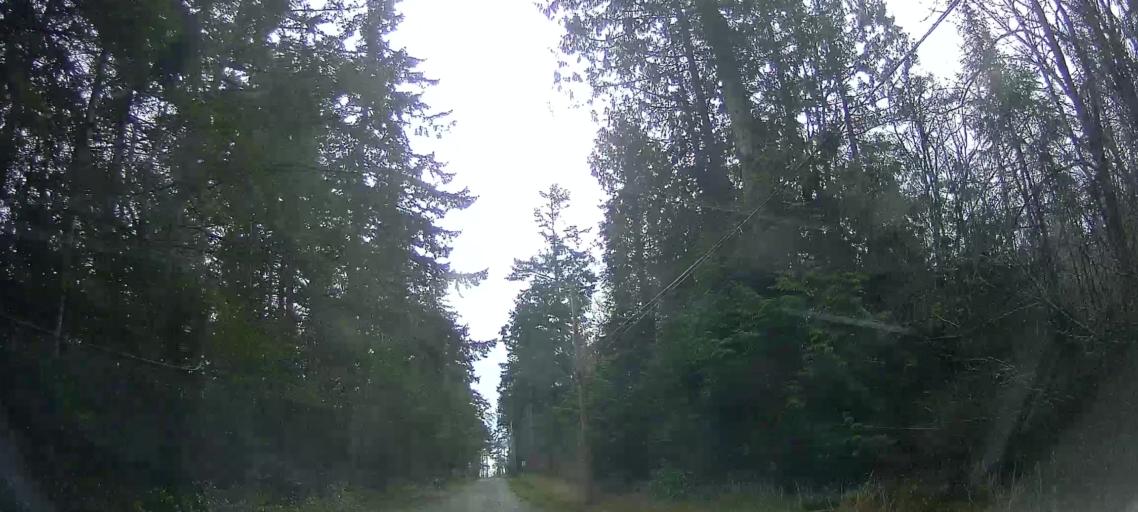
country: US
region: Washington
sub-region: Skagit County
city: Anacortes
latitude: 48.5794
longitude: -122.5526
